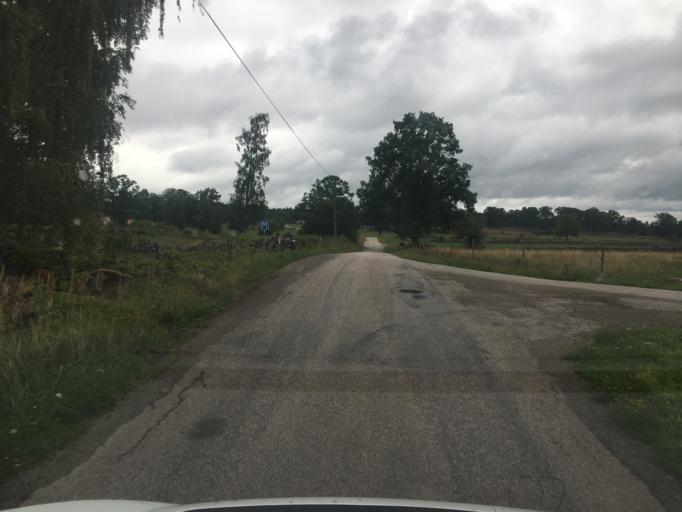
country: SE
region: Kronoberg
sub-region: Ljungby Kommun
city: Lagan
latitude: 56.9762
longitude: 14.0379
